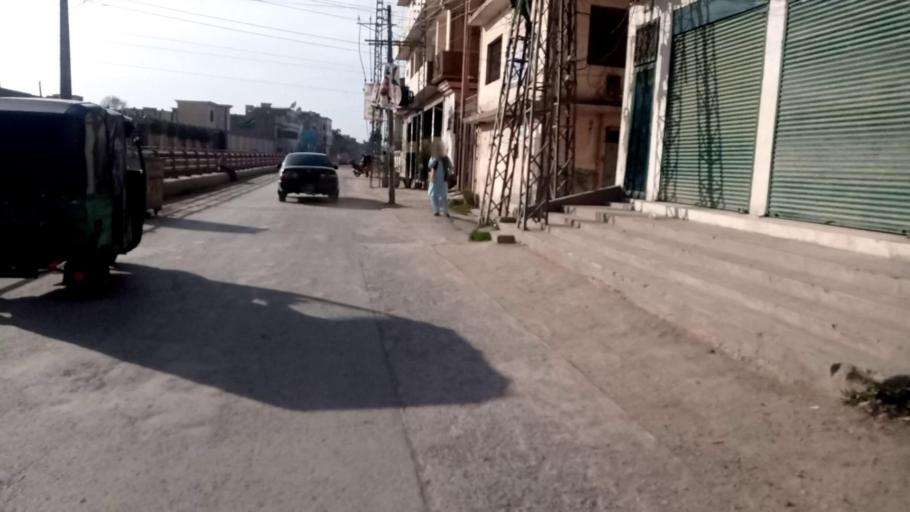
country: PK
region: Khyber Pakhtunkhwa
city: Peshawar
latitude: 34.0132
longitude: 71.6110
